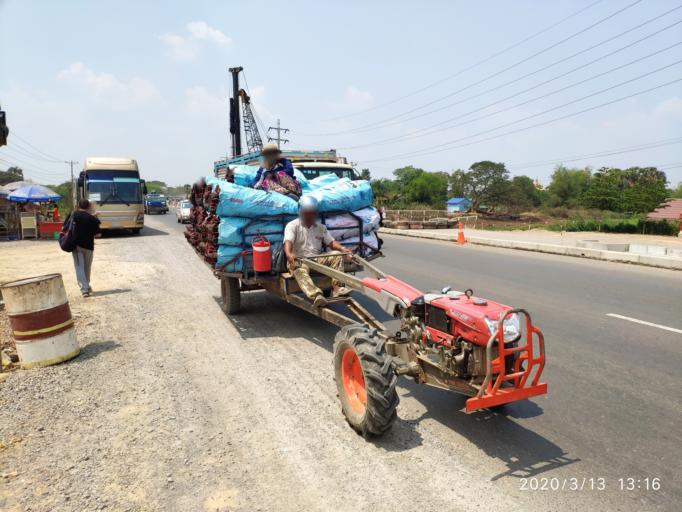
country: KH
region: Battambang
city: Battambang
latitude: 13.1418
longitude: 103.1198
